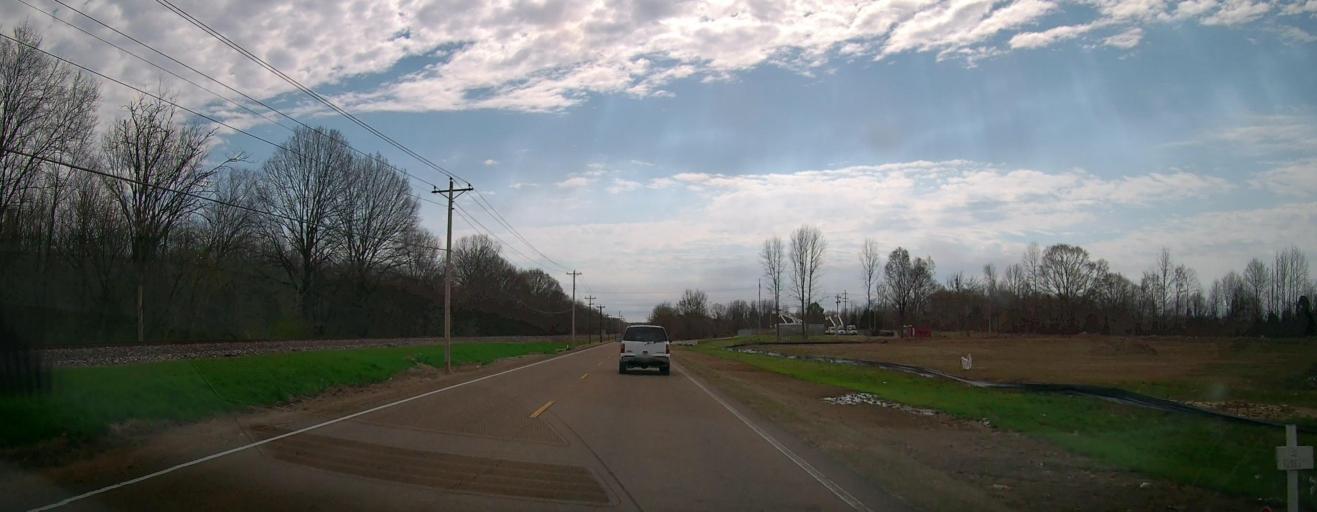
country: US
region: Mississippi
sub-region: De Soto County
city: Olive Branch
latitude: 34.9138
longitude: -89.7629
